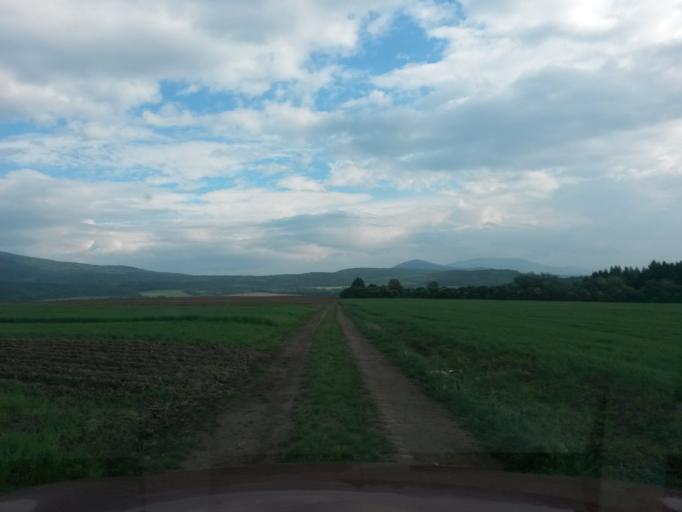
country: SK
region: Kosicky
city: Kosice
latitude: 48.7482
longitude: 21.4581
